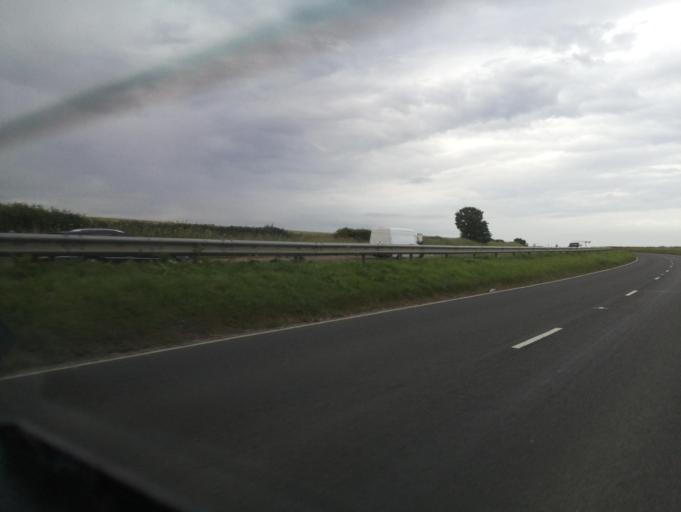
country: GB
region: England
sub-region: Dorset
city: Sherborne
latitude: 50.9462
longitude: -2.5436
